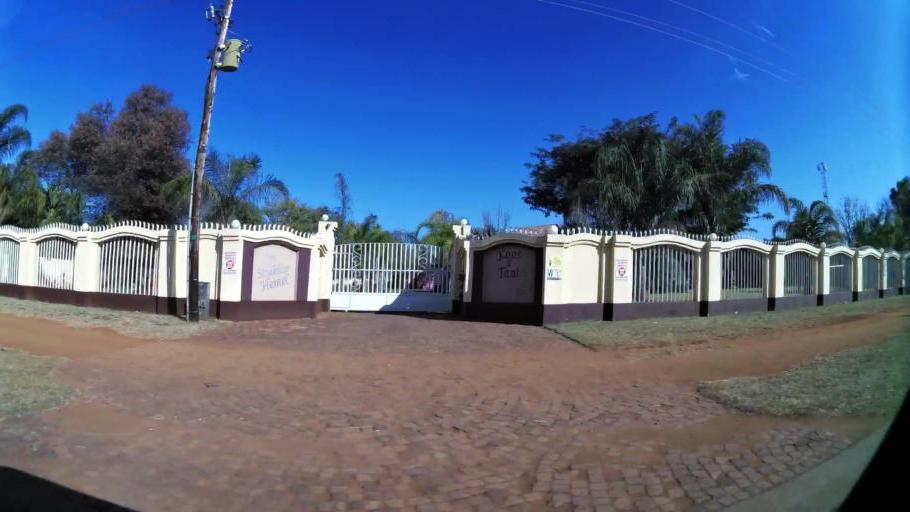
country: ZA
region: Gauteng
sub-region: City of Tshwane Metropolitan Municipality
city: Pretoria
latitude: -25.6567
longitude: 28.1315
